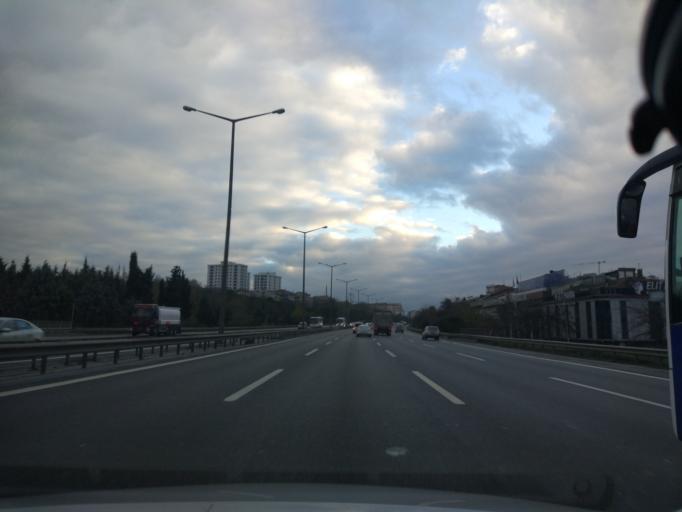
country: TR
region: Istanbul
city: Sultangazi
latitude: 41.0897
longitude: 28.8856
